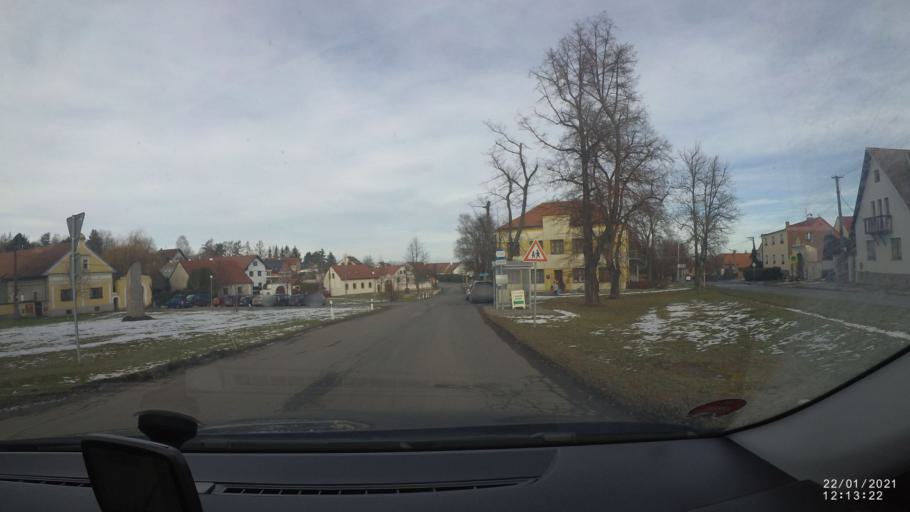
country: CZ
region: Plzensky
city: Dysina
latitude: 49.7546
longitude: 13.4846
